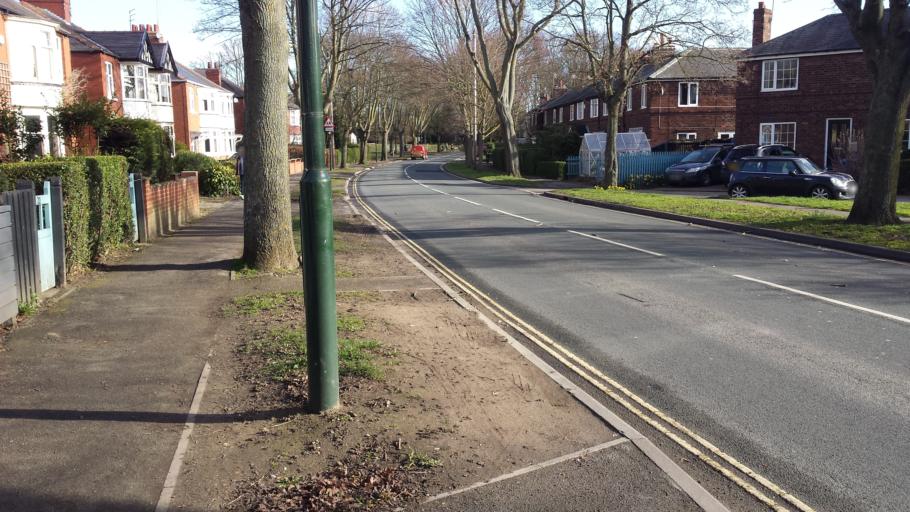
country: GB
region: England
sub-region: East Riding of Yorkshire
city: Beverley
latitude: 53.8378
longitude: -0.4331
